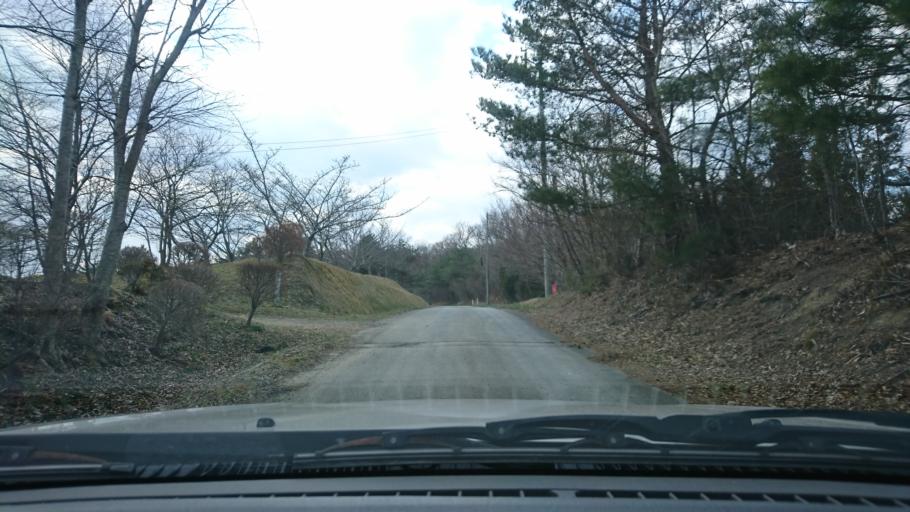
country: JP
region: Iwate
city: Ichinoseki
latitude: 38.8214
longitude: 141.2654
